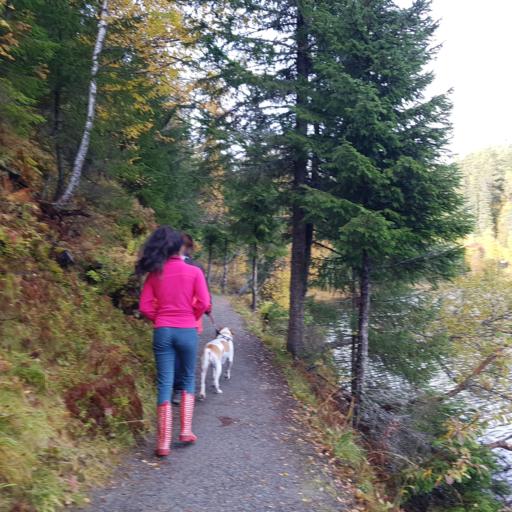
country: NO
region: Sor-Trondelag
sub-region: Trondheim
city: Trondheim
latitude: 63.4232
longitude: 10.2785
